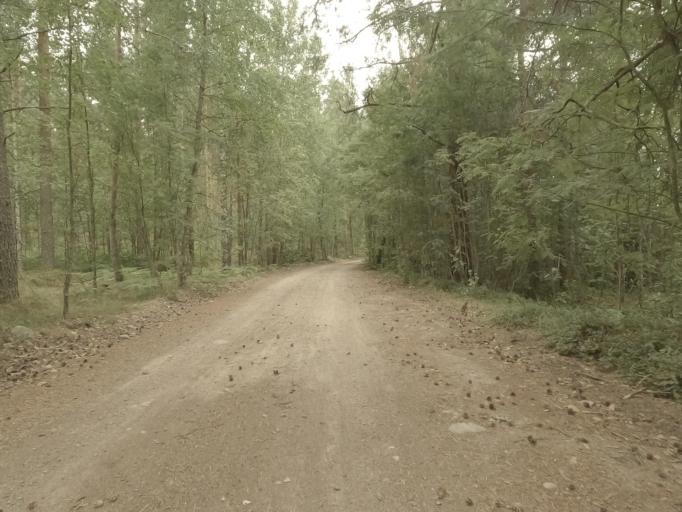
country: RU
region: Leningrad
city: Kamennogorsk
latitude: 60.9979
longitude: 29.1830
